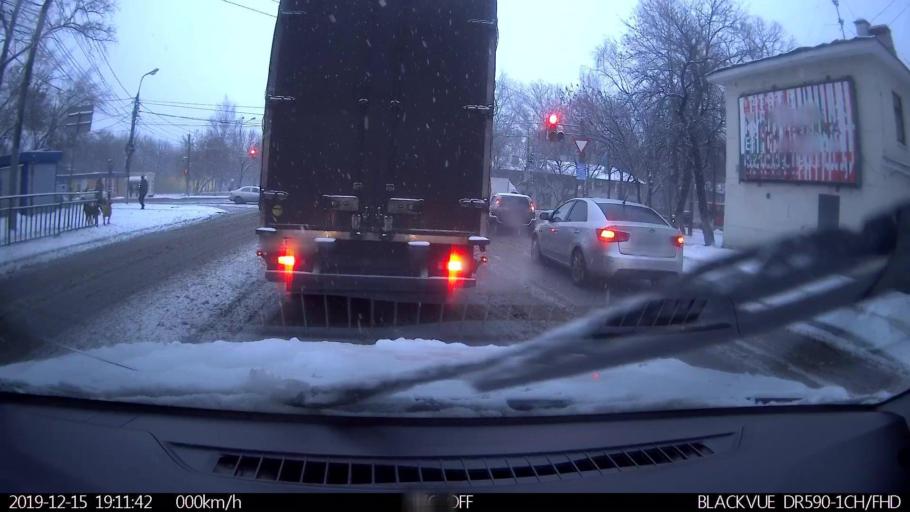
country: RU
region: Nizjnij Novgorod
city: Gorbatovka
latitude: 56.3444
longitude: 43.8397
